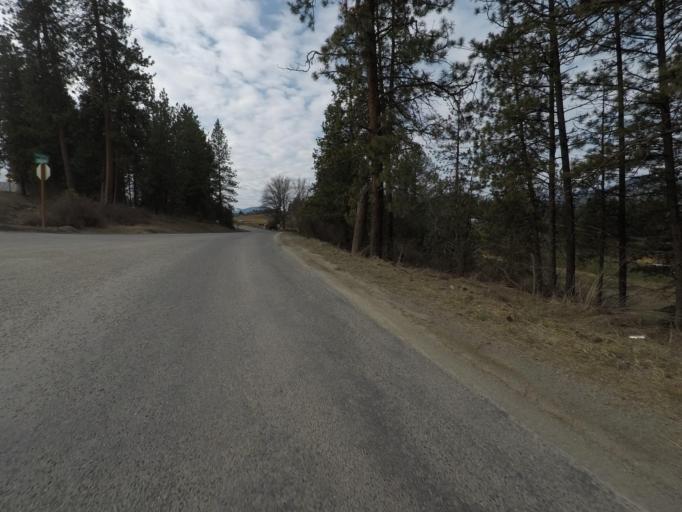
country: US
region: Washington
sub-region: Stevens County
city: Colville
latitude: 48.5285
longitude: -117.8797
